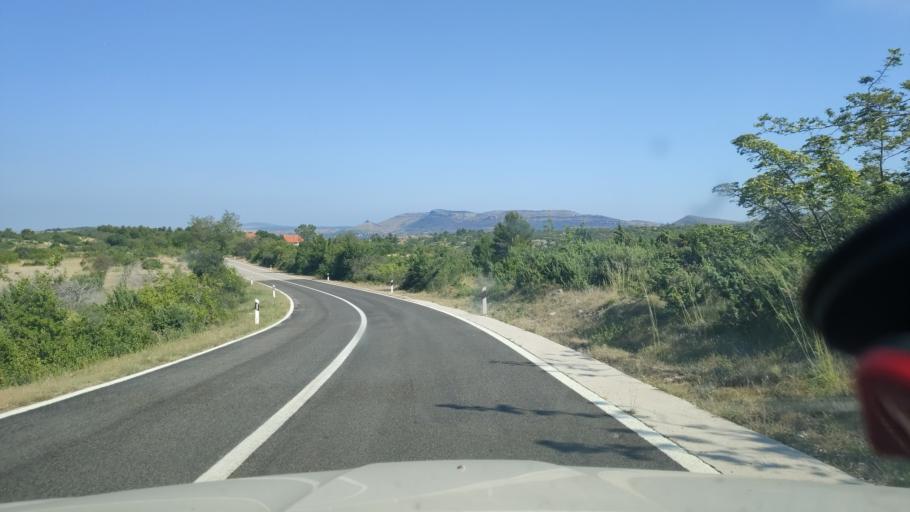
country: HR
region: Sibensko-Kniniska
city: Zaton
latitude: 43.9130
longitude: 15.8373
